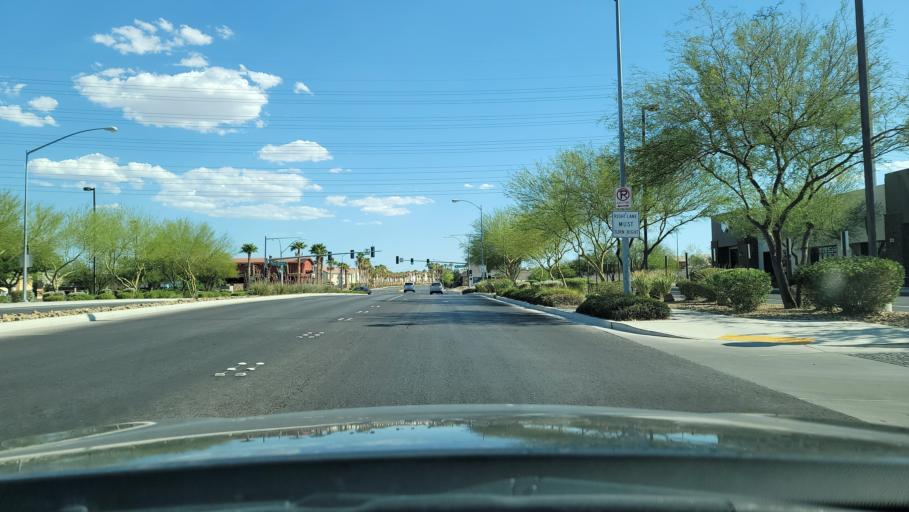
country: US
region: Nevada
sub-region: Clark County
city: Enterprise
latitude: 36.0568
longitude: -115.2521
